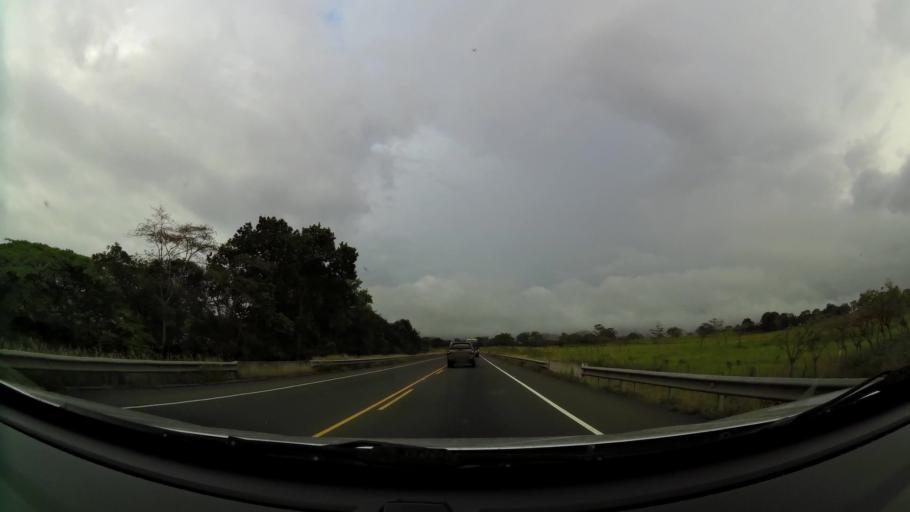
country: CR
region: Alajuela
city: Carrillos
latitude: 9.9653
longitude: -84.2969
